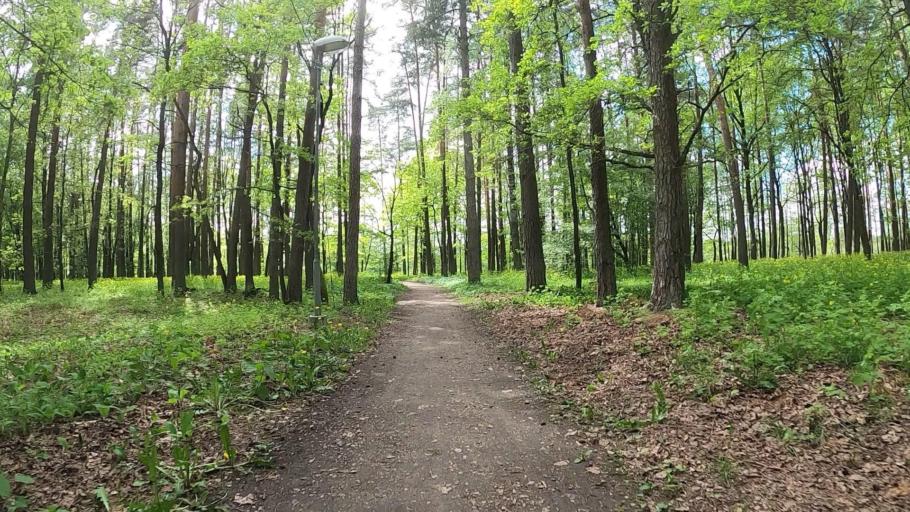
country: LV
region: Babite
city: Pinki
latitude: 56.8786
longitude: 23.9422
